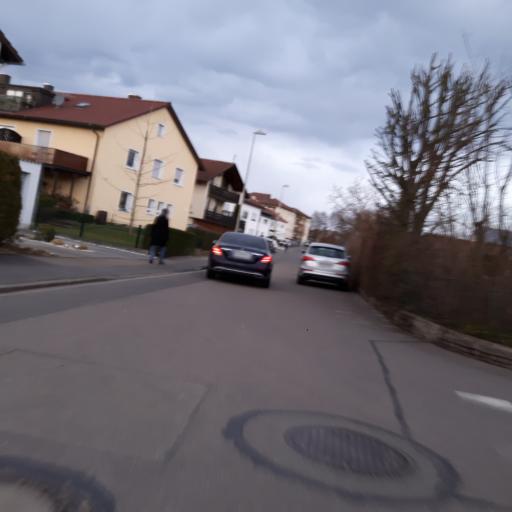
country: DE
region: Baden-Wuerttemberg
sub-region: Regierungsbezirk Stuttgart
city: Pleidelsheim
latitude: 48.9631
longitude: 9.2024
